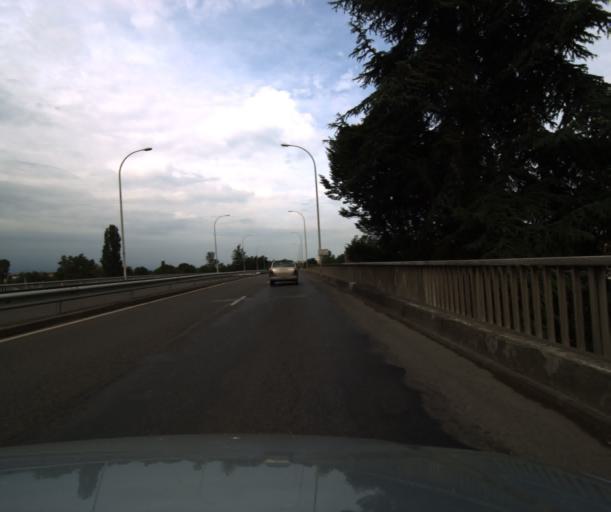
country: FR
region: Midi-Pyrenees
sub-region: Departement des Hautes-Pyrenees
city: Tarbes
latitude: 43.2295
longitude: 0.0932
